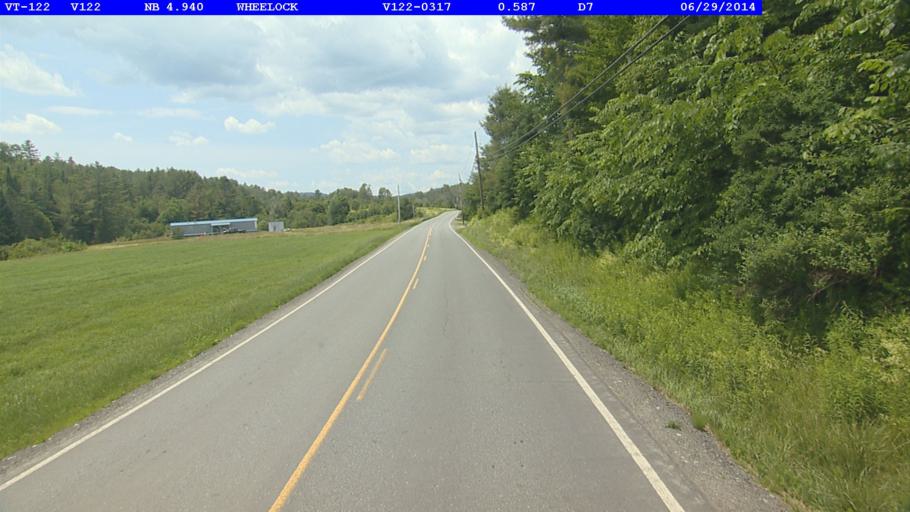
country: US
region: Vermont
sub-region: Caledonia County
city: Lyndonville
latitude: 44.5824
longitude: -72.0747
